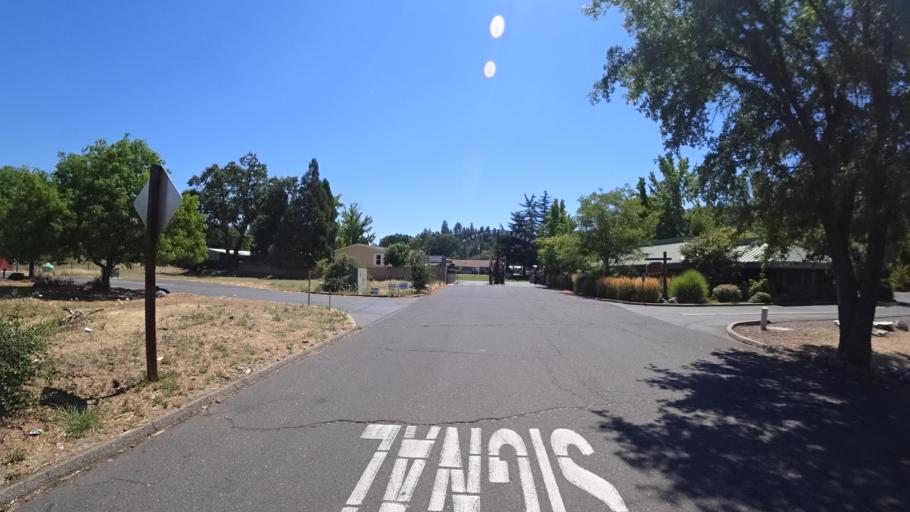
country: US
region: California
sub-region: Calaveras County
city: Murphys
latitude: 38.1387
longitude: -120.4552
